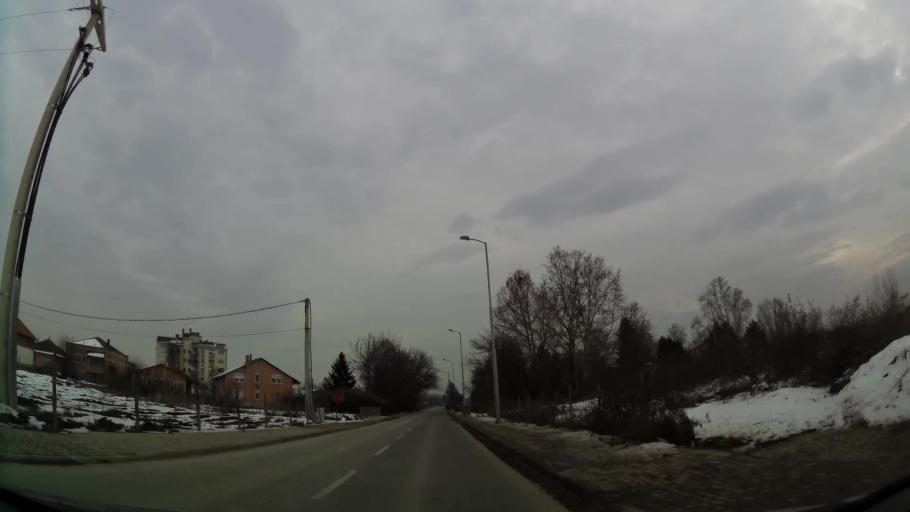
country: MK
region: Butel
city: Butel
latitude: 42.0372
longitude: 21.4428
